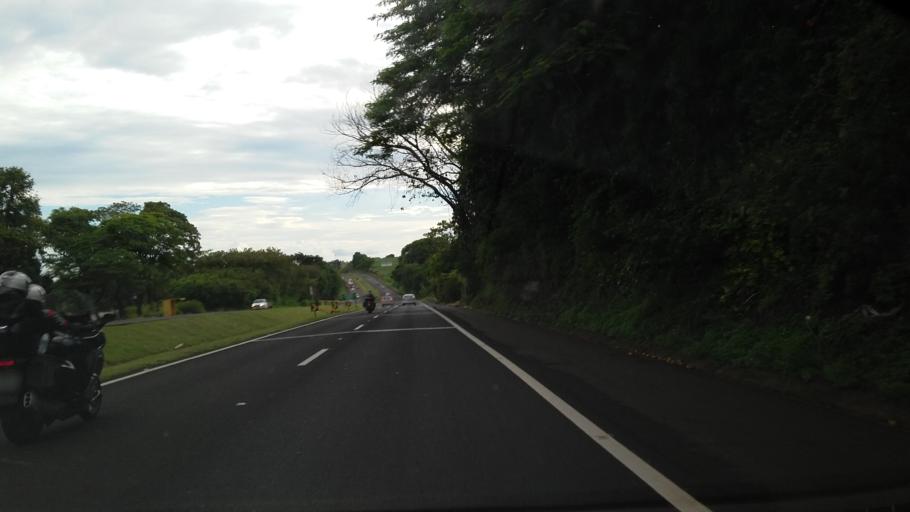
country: BR
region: Parana
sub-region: Paicandu
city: Paicandu
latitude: -23.5094
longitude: -52.0233
